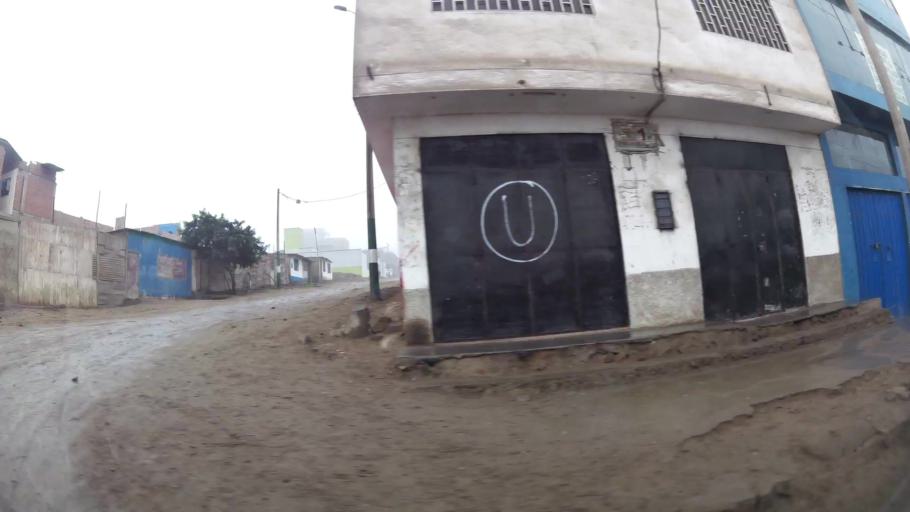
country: PE
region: Lima
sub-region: Lima
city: Santa Rosa
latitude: -11.8320
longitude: -77.1460
